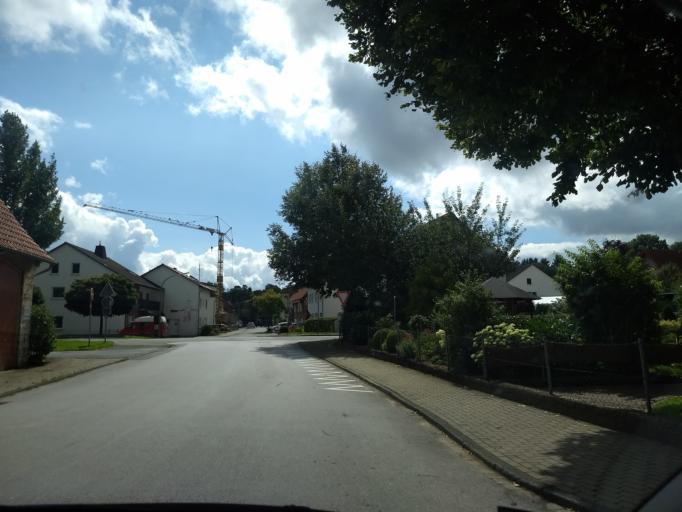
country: DE
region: North Rhine-Westphalia
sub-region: Regierungsbezirk Detmold
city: Buren
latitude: 51.5420
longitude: 8.5250
